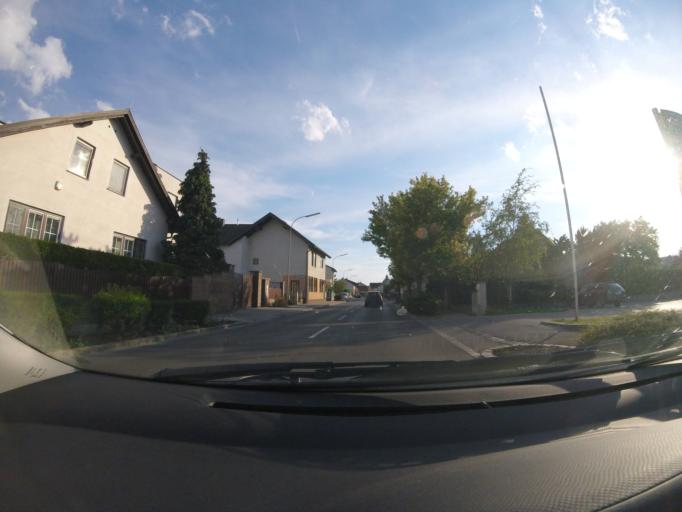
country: AT
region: Lower Austria
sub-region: Politischer Bezirk Wiener Neustadt
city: Zillingdorf
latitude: 47.8536
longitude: 16.3134
